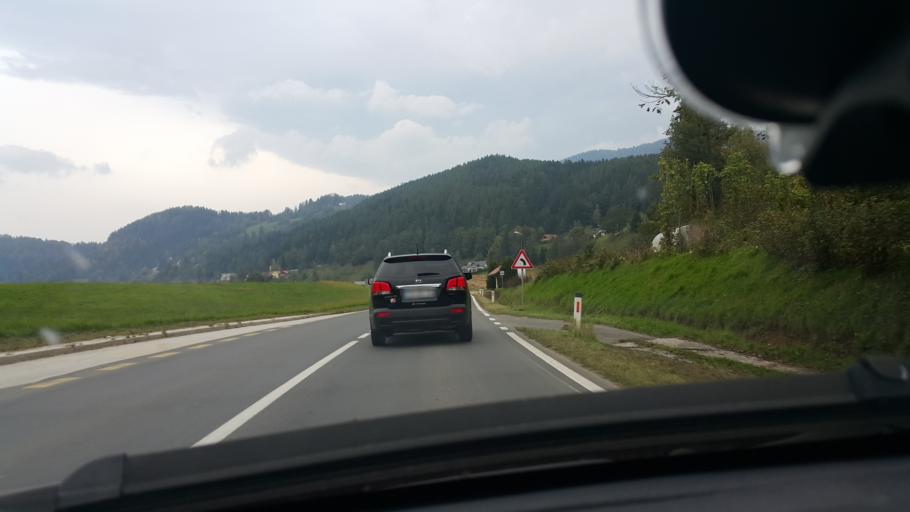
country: SI
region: Radlje ob Dravi
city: Radlje ob Dravi
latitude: 46.6064
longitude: 15.2494
